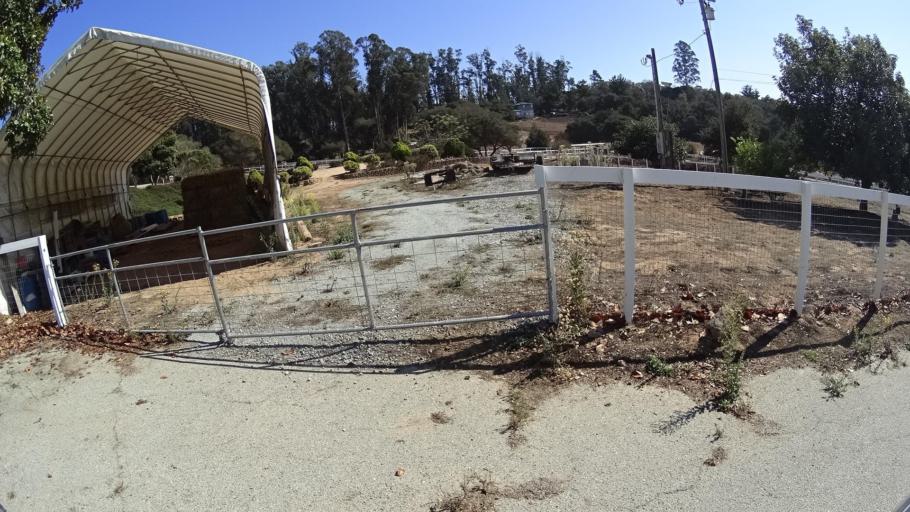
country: US
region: California
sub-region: Monterey County
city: Prunedale
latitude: 36.8208
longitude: -121.6541
